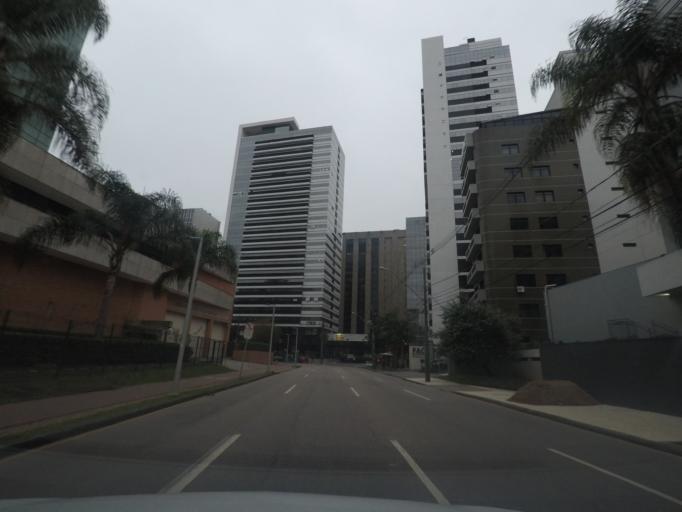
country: BR
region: Parana
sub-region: Curitiba
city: Curitiba
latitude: -25.4214
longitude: -49.2683
